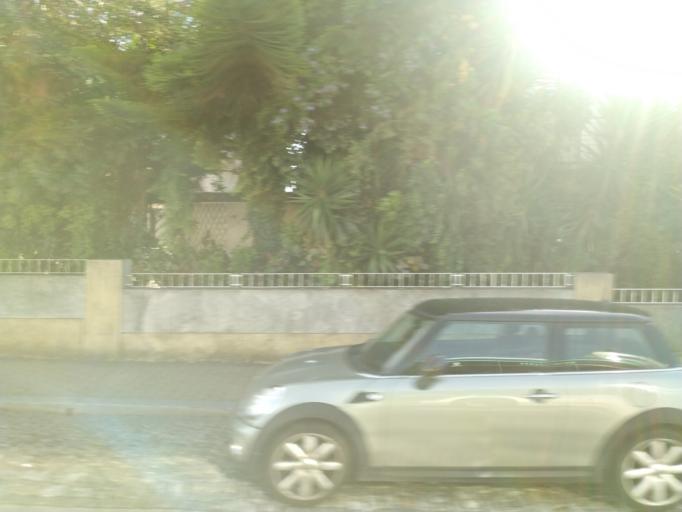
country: PT
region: Porto
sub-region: Vila Nova de Gaia
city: Vilar de Andorinho
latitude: 41.1088
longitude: -8.5958
